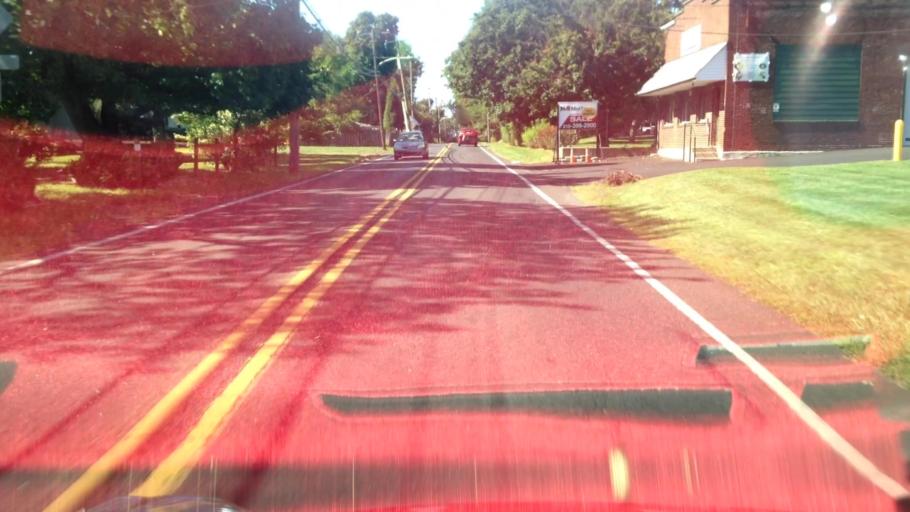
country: US
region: Pennsylvania
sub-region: Bucks County
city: Hulmeville
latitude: 40.1273
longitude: -74.8947
